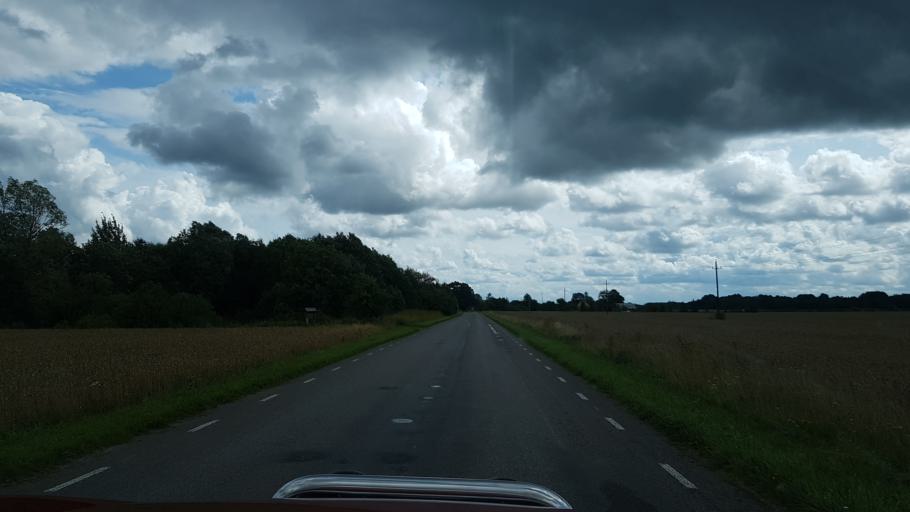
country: EE
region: Laeaene
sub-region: Lihula vald
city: Lihula
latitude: 58.7142
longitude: 24.0004
